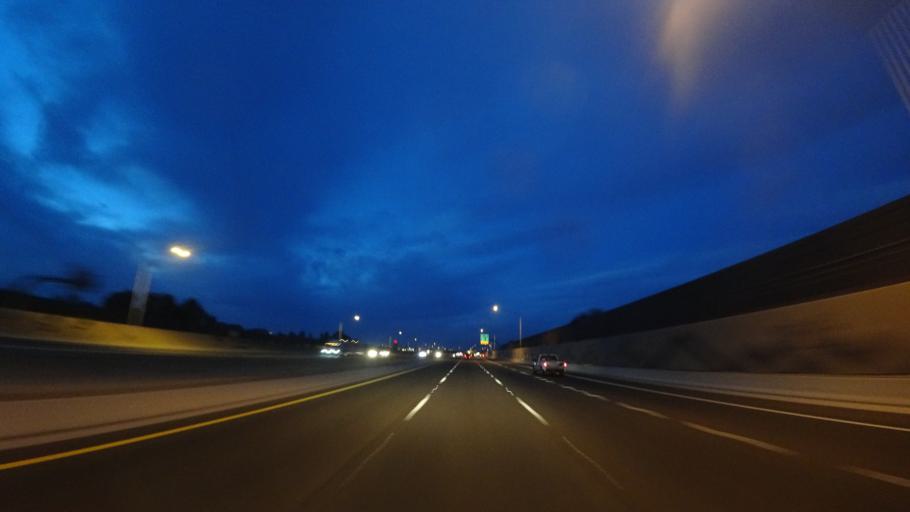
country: US
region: Arizona
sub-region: Maricopa County
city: Sun City West
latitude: 33.6317
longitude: -112.4179
